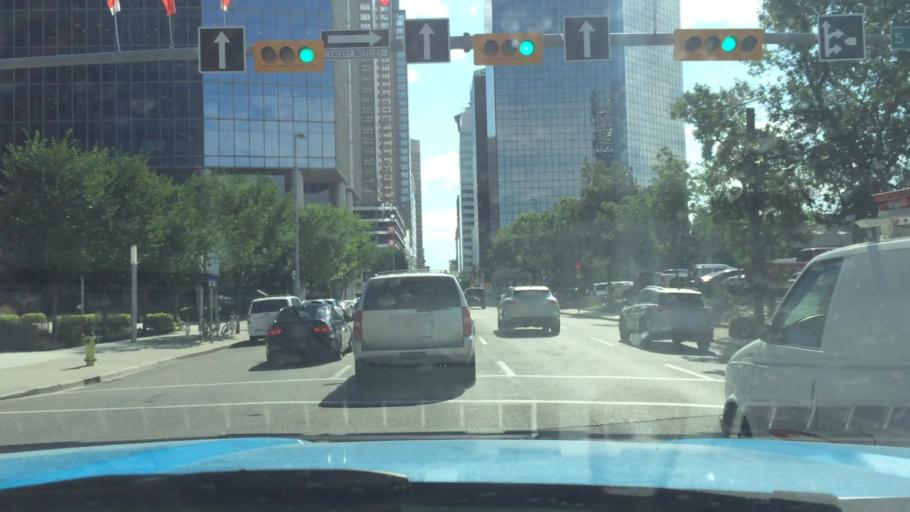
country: CA
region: Alberta
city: Calgary
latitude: 51.0448
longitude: -114.0738
